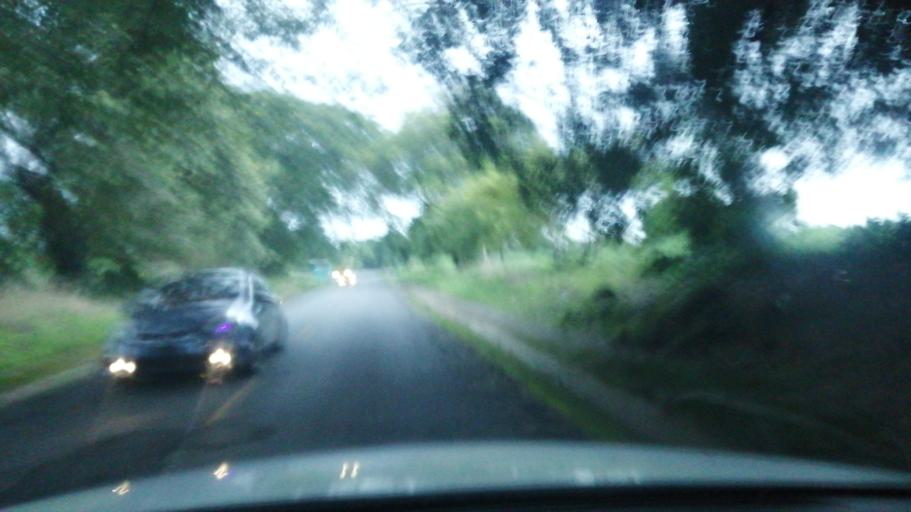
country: PA
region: Chiriqui
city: Alanje
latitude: 8.3961
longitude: -82.4963
